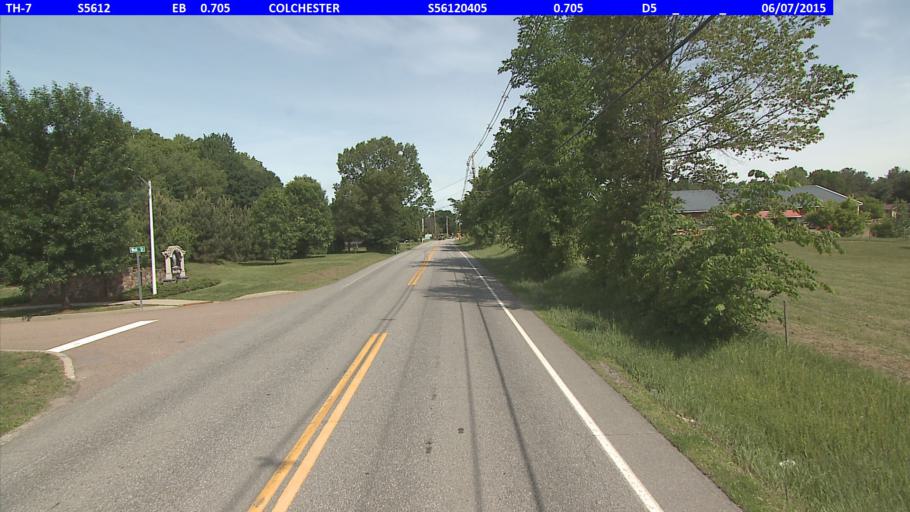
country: US
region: Vermont
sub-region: Chittenden County
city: Colchester
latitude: 44.5200
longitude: -73.1500
